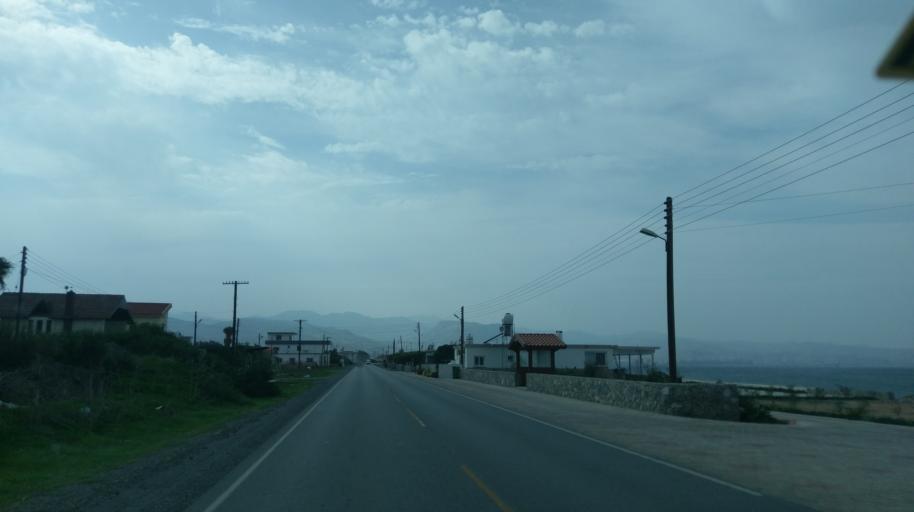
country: CY
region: Lefkosia
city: Lefka
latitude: 35.1511
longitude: 32.8578
